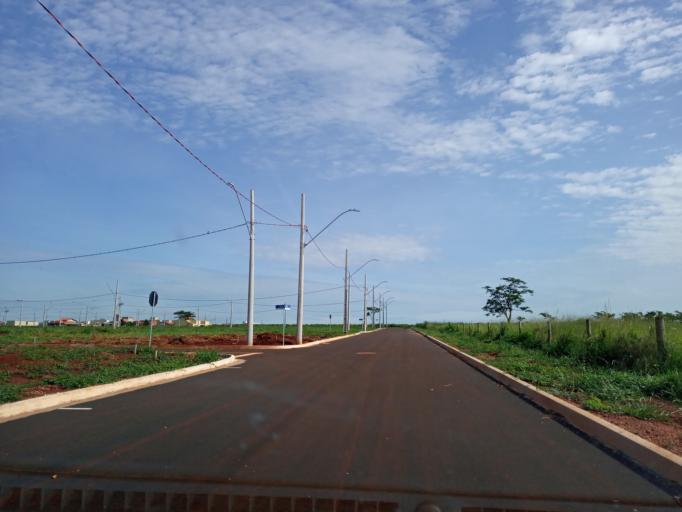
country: BR
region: Goias
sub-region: Itumbiara
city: Itumbiara
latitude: -18.4314
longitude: -49.1799
